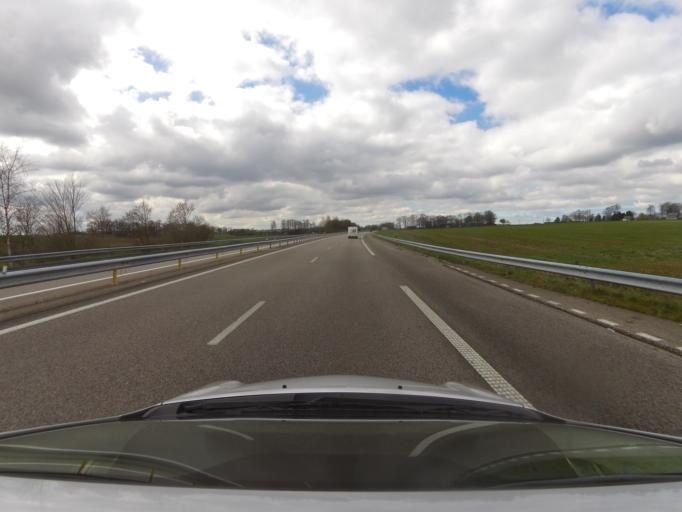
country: FR
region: Haute-Normandie
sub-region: Departement de la Seine-Maritime
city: Beuzeville-la-Grenier
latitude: 49.5805
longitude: 0.4317
